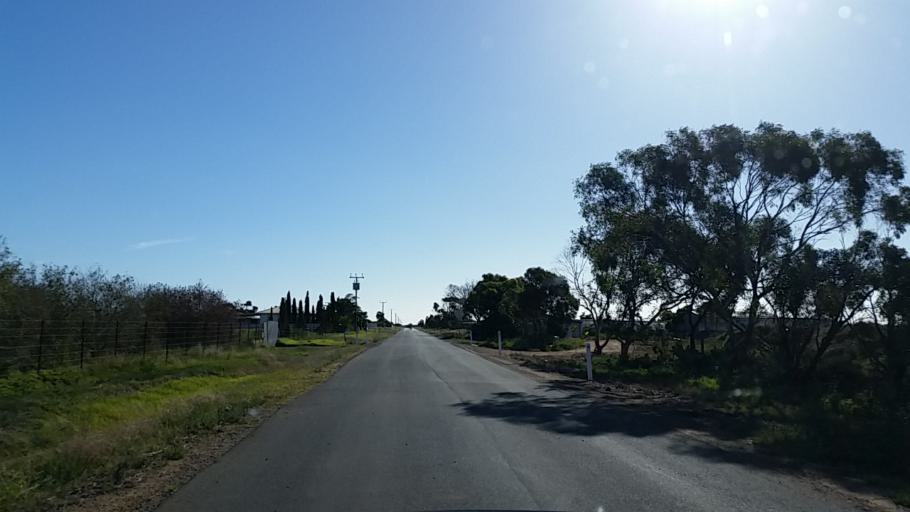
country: AU
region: South Australia
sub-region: Playford
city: Virginia
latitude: -34.6710
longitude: 138.5352
